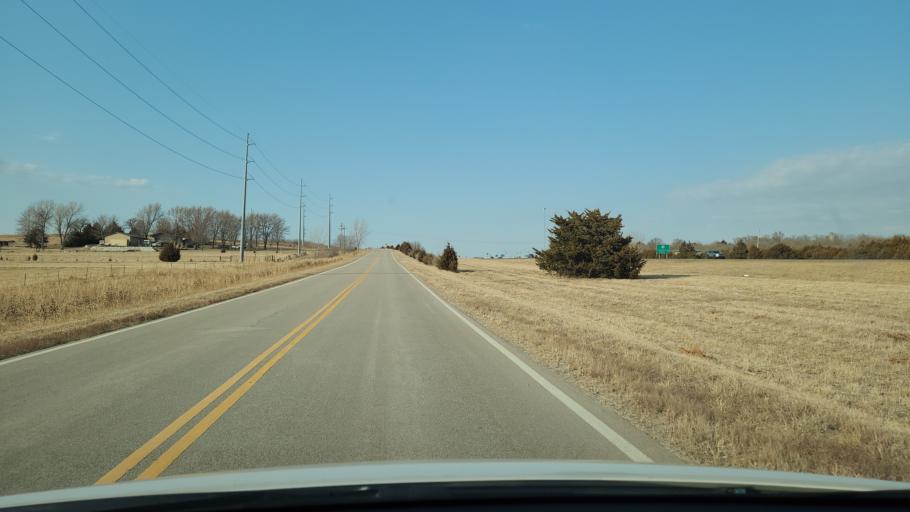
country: US
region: Kansas
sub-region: Douglas County
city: Lawrence
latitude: 38.9645
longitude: -95.3349
